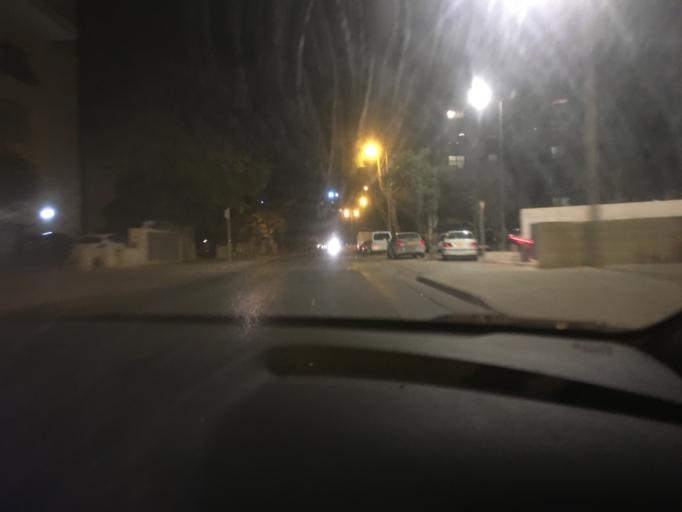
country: IL
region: Jerusalem
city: Jerusalem
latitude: 31.7589
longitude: 35.2253
